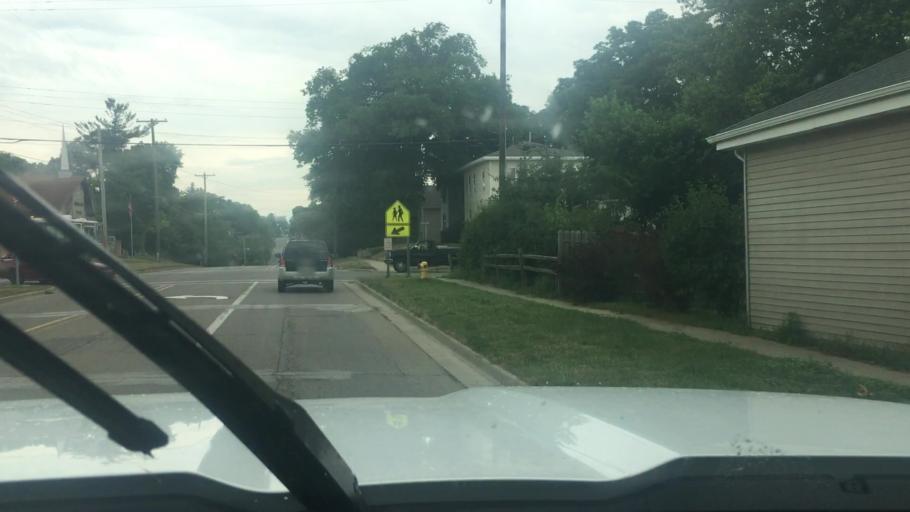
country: US
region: Michigan
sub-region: Ionia County
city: Ionia
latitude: 42.9874
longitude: -85.0540
